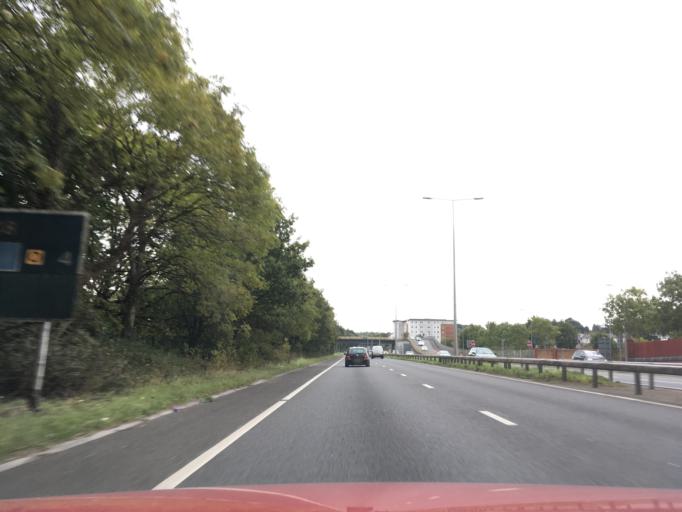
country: GB
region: Wales
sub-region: Cardiff
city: Cardiff
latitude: 51.5056
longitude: -3.1910
